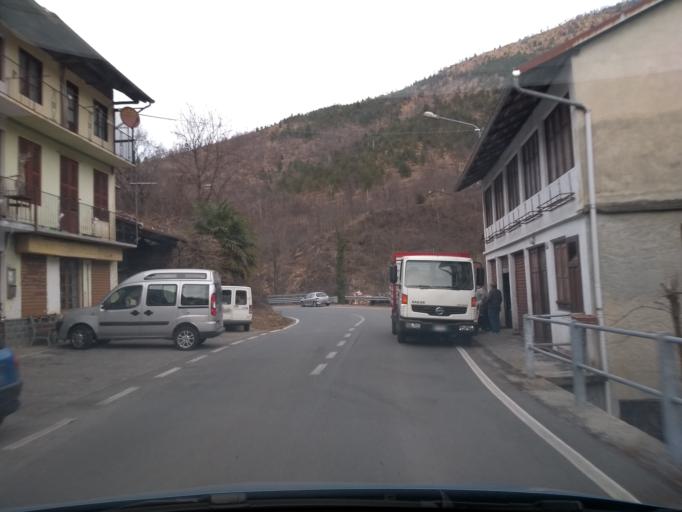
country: IT
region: Piedmont
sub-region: Provincia di Torino
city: La Villa
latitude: 45.2396
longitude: 7.4373
